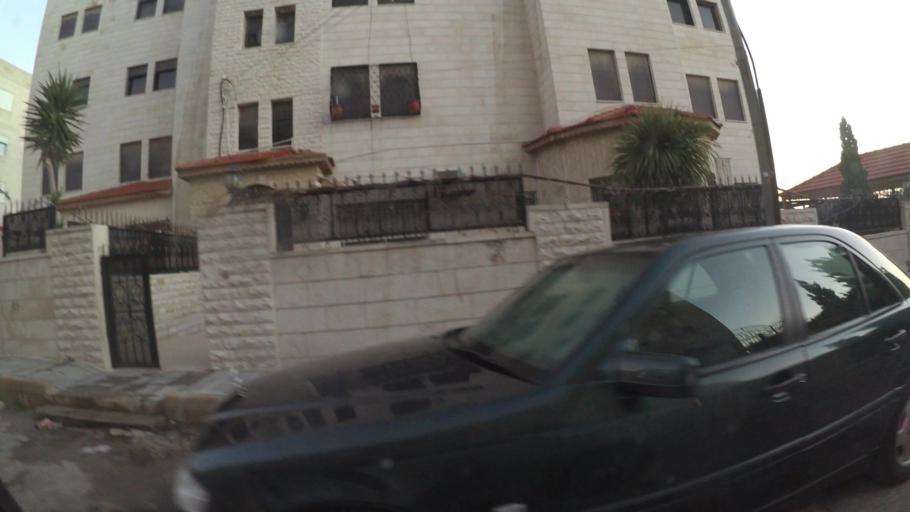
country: JO
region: Amman
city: Al Jubayhah
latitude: 31.9996
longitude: 35.8542
